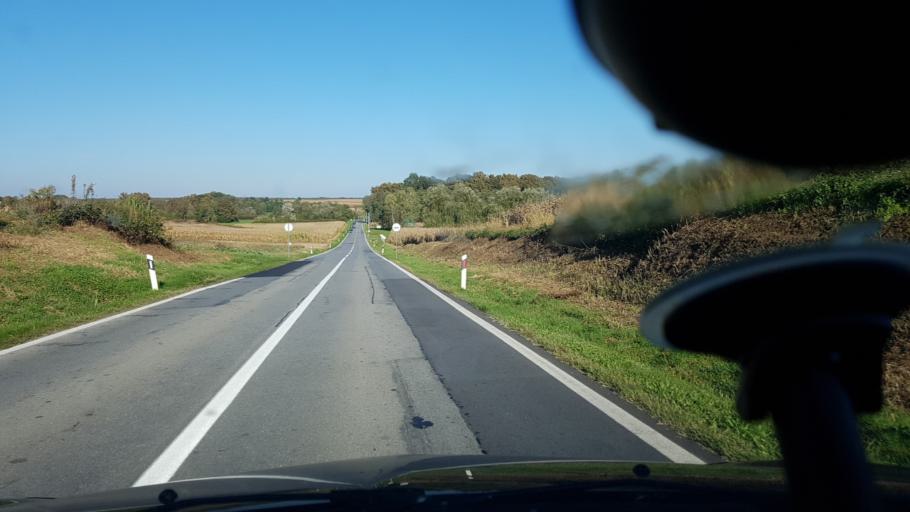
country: HR
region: Bjelovarsko-Bilogorska
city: Gudovac
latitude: 45.8270
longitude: 16.7479
